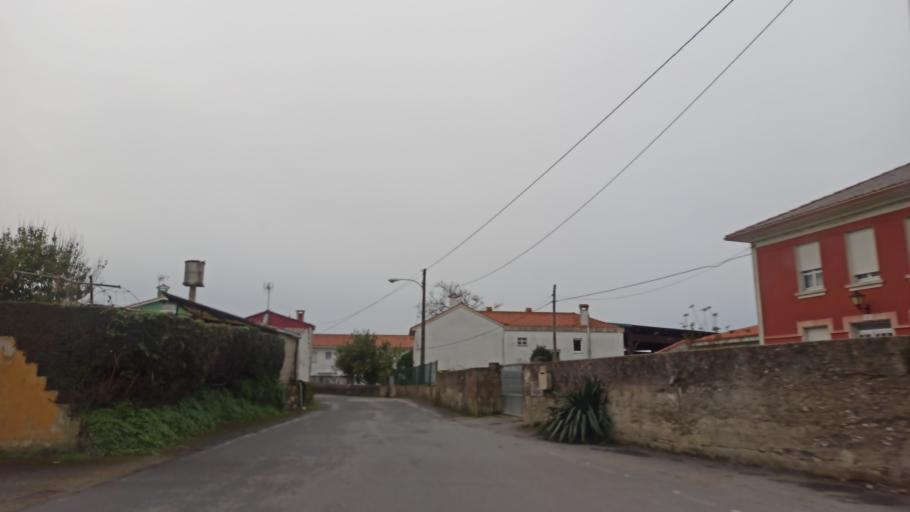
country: ES
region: Galicia
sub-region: Provincia da Coruna
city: Oleiros
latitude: 43.3955
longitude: -8.3214
